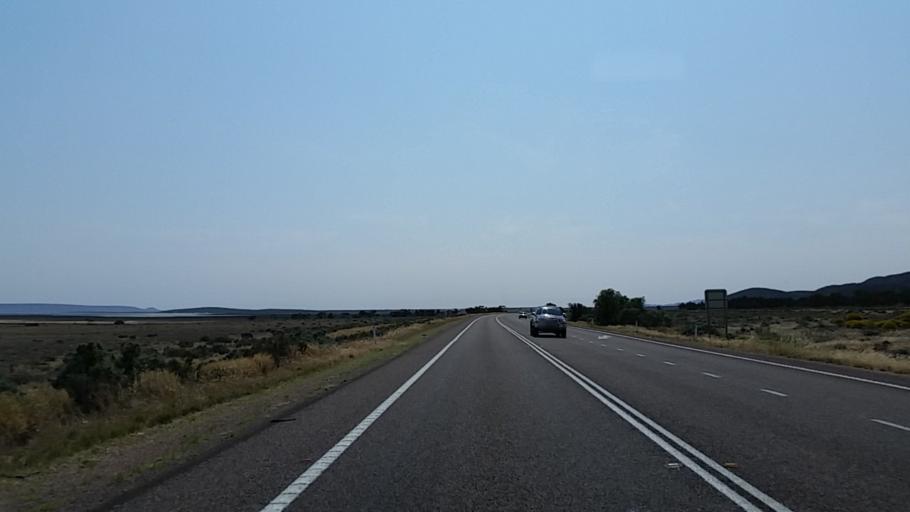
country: AU
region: South Australia
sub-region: Port Augusta
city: Port Augusta
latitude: -32.7859
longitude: 137.9559
